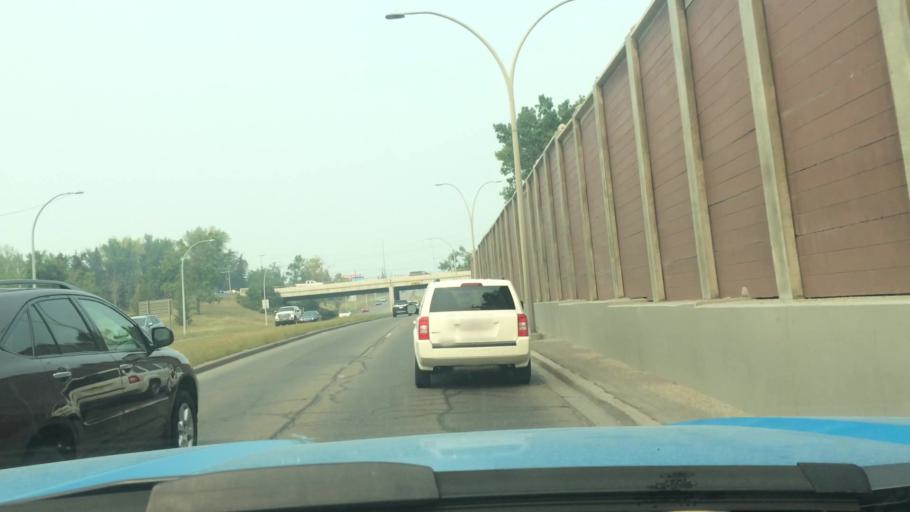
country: CA
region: Alberta
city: Calgary
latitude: 51.0654
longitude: -114.1178
